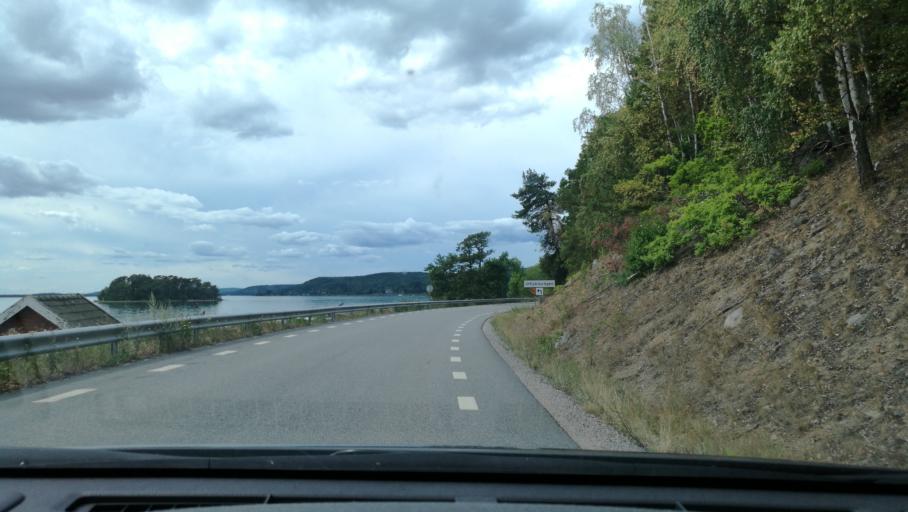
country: SE
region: OEstergoetland
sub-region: Norrkopings Kommun
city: Krokek
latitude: 58.6605
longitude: 16.3745
